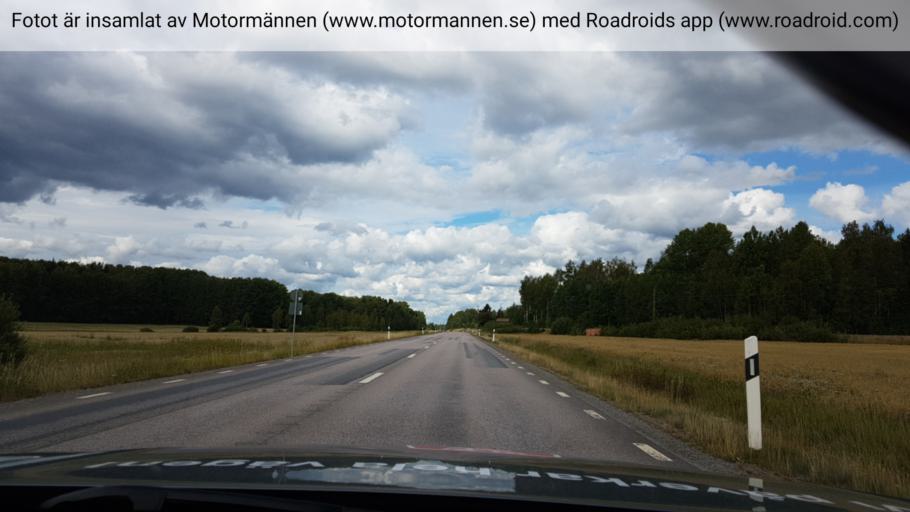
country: SE
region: Uppsala
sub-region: Heby Kommun
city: Morgongava
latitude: 59.9201
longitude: 16.9945
